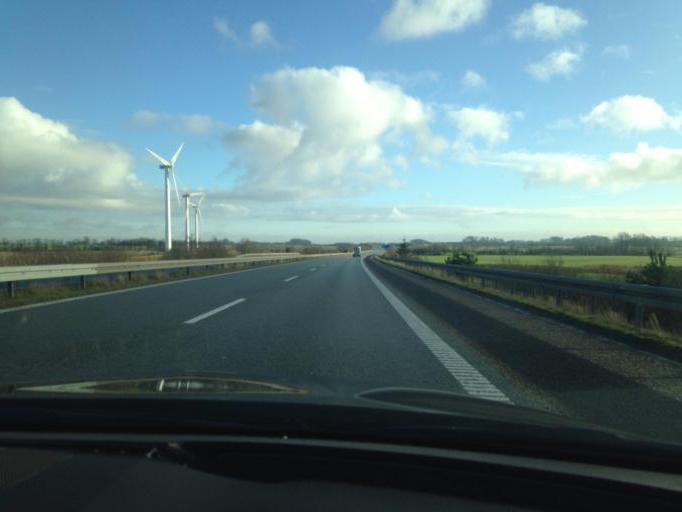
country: DK
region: South Denmark
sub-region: Vejen Kommune
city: Brorup
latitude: 55.5090
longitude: 8.9927
